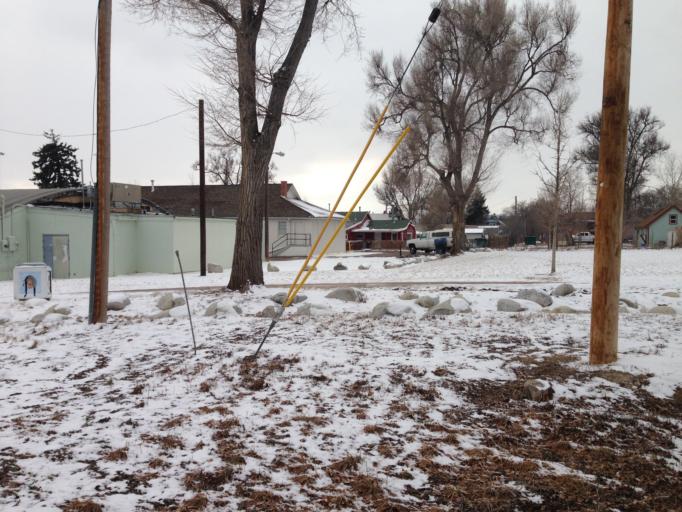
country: US
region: Colorado
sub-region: Adams County
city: Westminster
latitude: 39.8295
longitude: -105.0388
